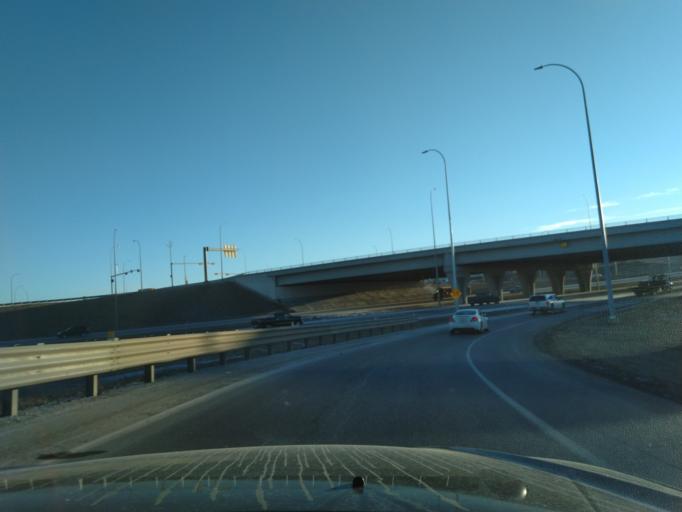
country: CA
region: Alberta
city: Calgary
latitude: 51.1579
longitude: -114.1156
